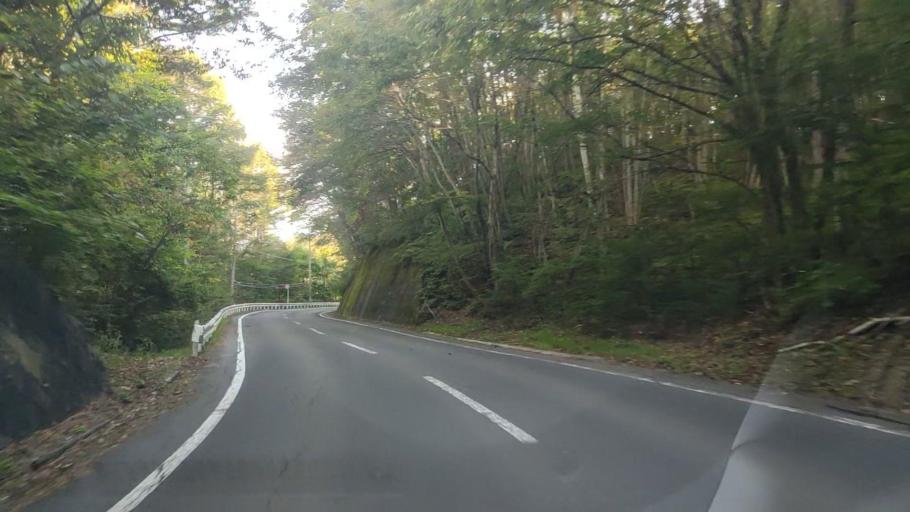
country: JP
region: Nagano
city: Suzaka
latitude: 36.5524
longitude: 138.5576
